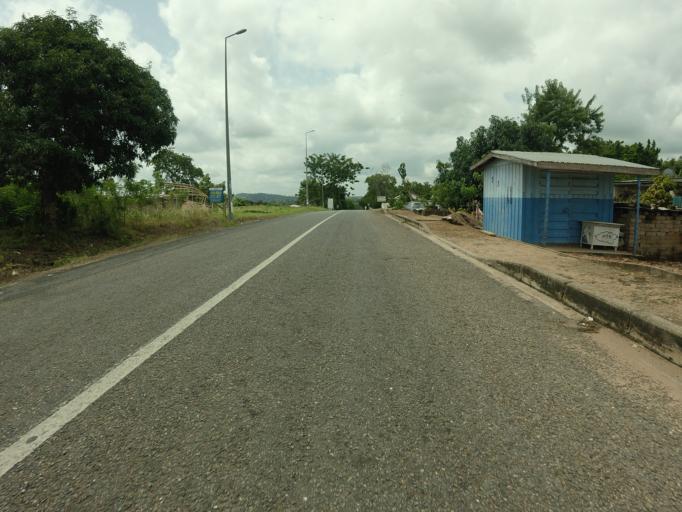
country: GH
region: Volta
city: Ho
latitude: 6.5943
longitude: 0.4768
